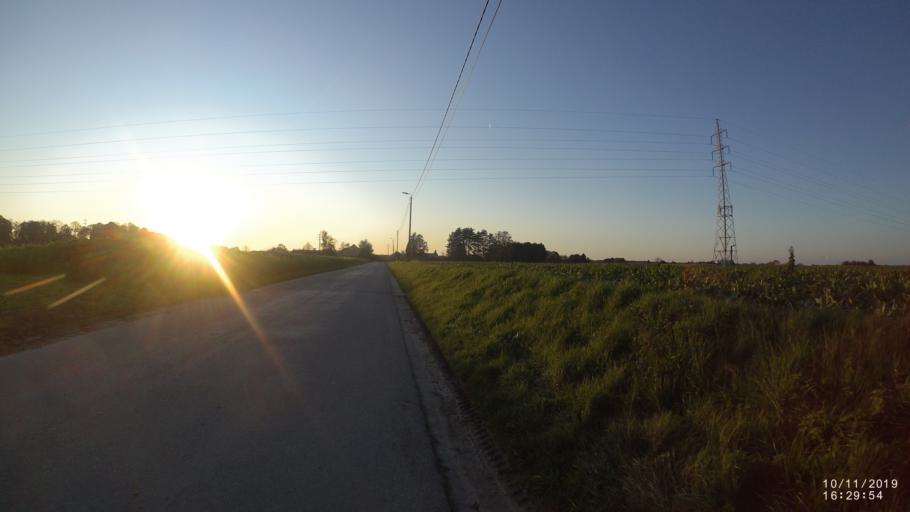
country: BE
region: Flanders
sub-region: Provincie Vlaams-Brabant
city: Lubbeek
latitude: 50.8730
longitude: 4.8043
